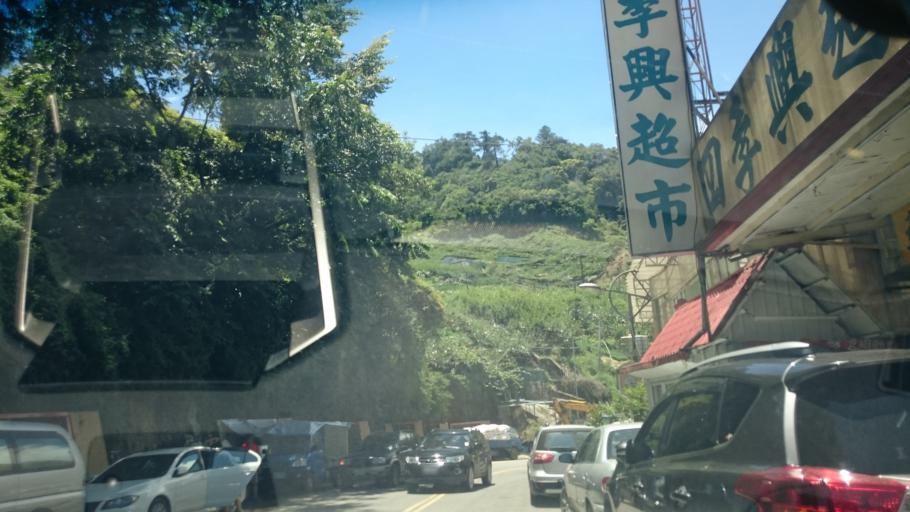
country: TW
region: Taiwan
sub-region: Nantou
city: Puli
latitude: 24.2540
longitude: 121.2541
